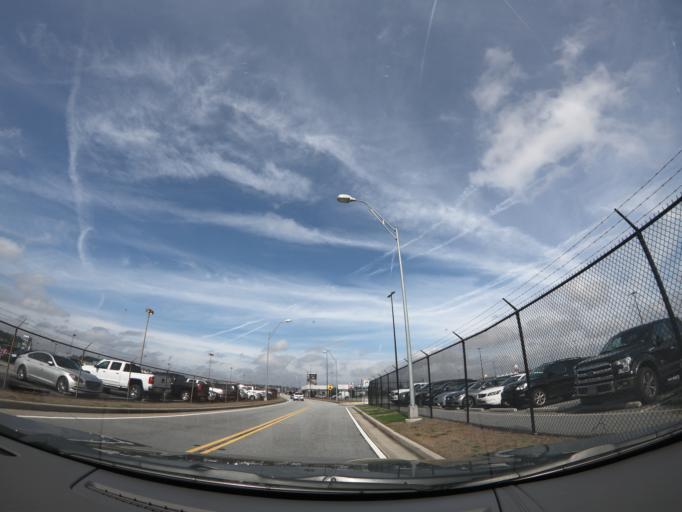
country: US
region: Georgia
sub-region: Fulton County
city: College Park
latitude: 33.6321
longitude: -84.4537
